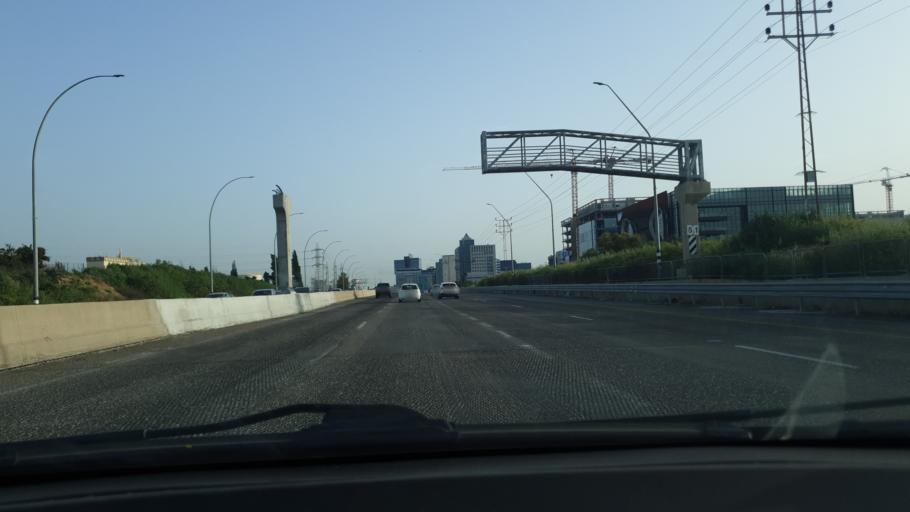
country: IL
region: Central District
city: Ra'anana
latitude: 32.2038
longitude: 34.8843
